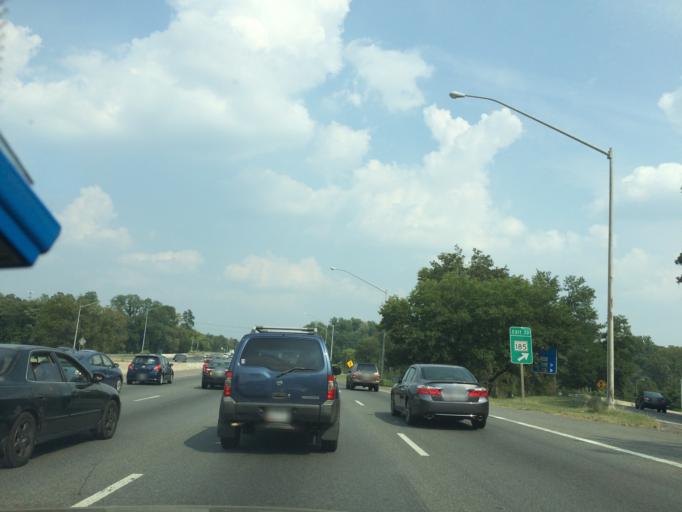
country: US
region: Maryland
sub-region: Montgomery County
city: South Kensington
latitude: 39.0051
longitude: -77.0809
